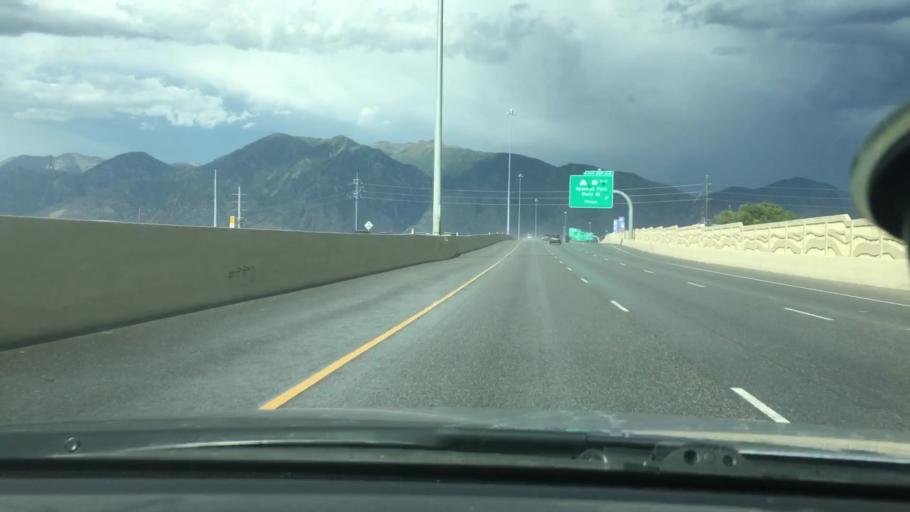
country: US
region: Utah
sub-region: Utah County
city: Spanish Fork
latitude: 40.1201
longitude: -111.6621
